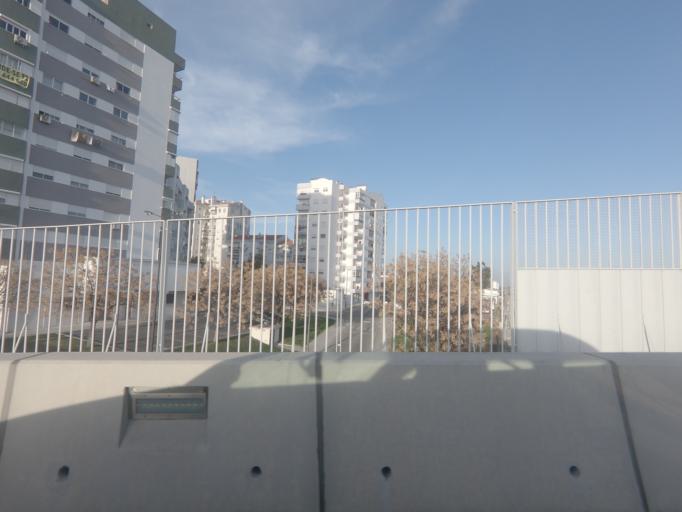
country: PT
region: Castelo Branco
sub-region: Castelo Branco
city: Castelo Branco
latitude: 39.8190
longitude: -7.4876
